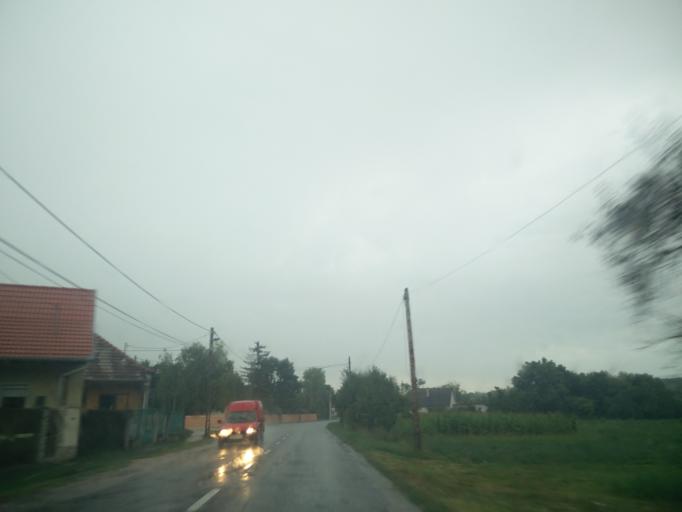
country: HU
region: Fejer
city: Lovasbereny
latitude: 47.3690
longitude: 18.5776
